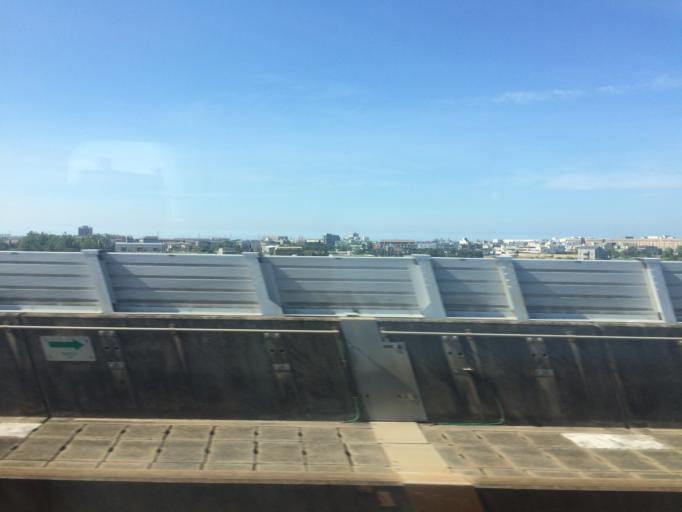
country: TW
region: Taiwan
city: Taoyuan City
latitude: 24.9573
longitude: 121.1539
